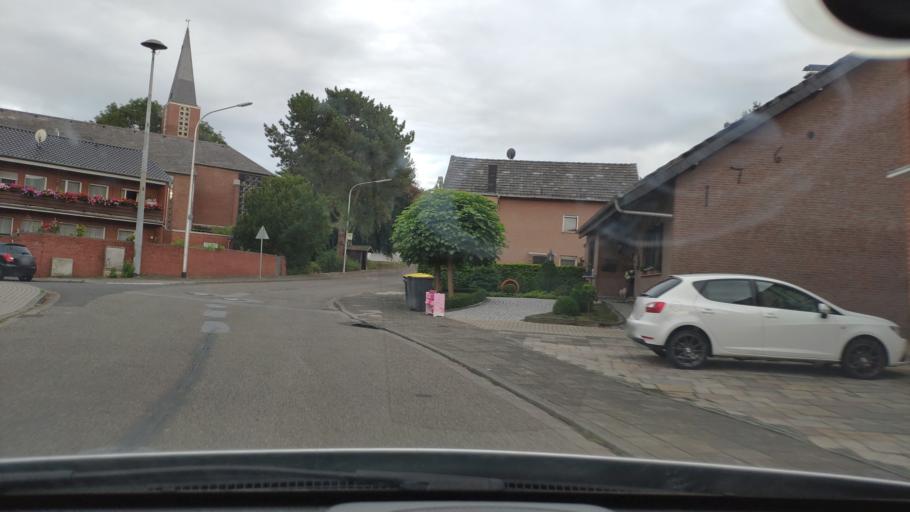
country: DE
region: North Rhine-Westphalia
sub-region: Regierungsbezirk Koln
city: Heinsberg
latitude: 51.0493
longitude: 6.1254
